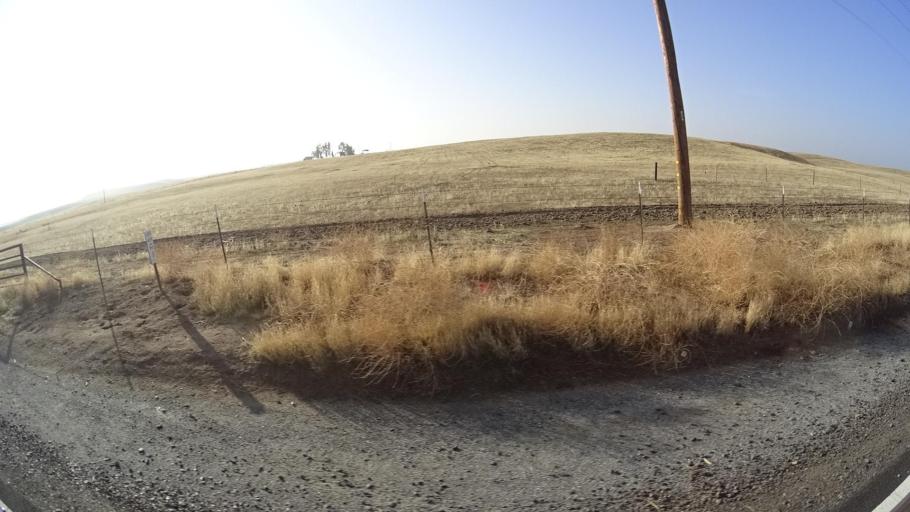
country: US
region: California
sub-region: Tulare County
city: Richgrove
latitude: 35.7620
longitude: -119.0358
